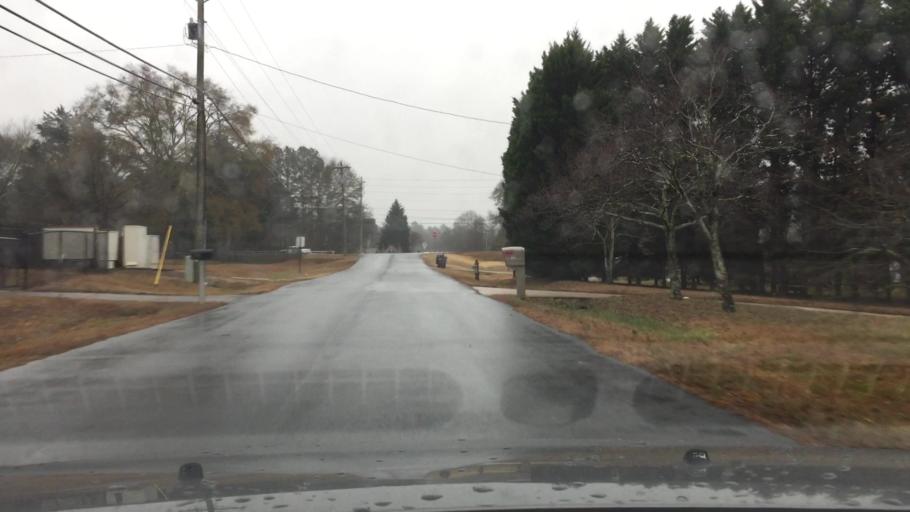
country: US
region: Georgia
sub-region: Cobb County
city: Fair Oaks
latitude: 33.9037
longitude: -84.6203
